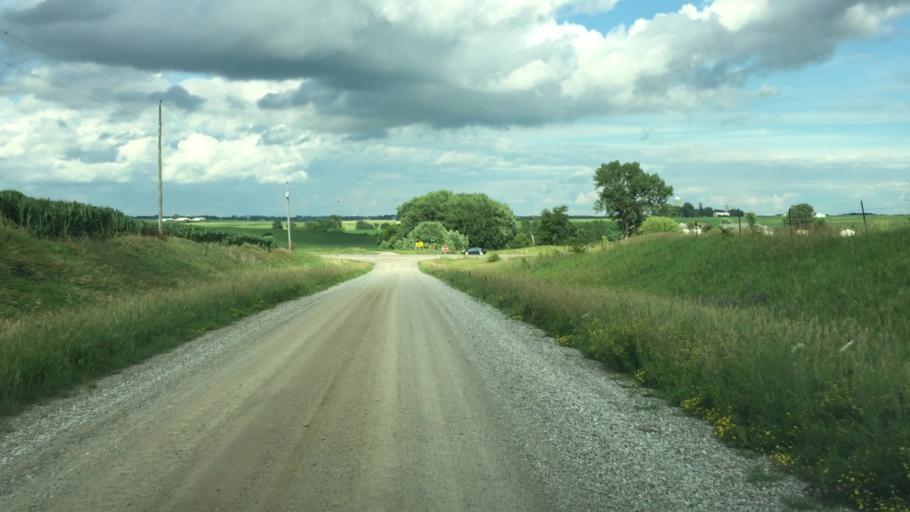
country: US
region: Iowa
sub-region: Jasper County
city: Monroe
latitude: 41.5663
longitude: -93.0990
